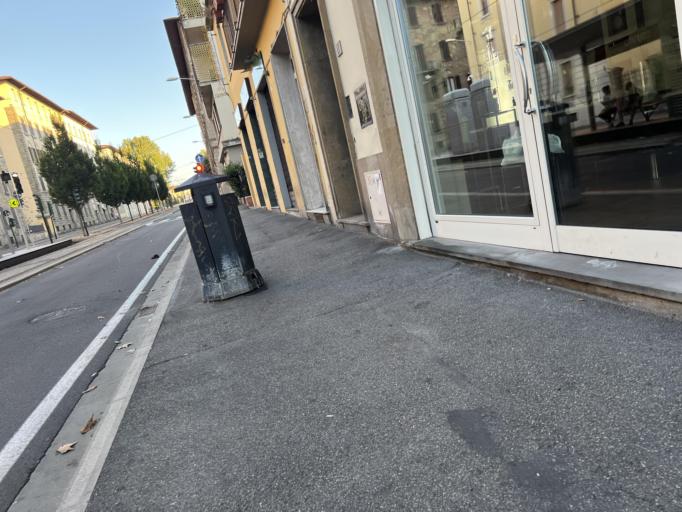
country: IT
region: Tuscany
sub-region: Province of Florence
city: Florence
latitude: 43.7858
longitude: 11.2507
